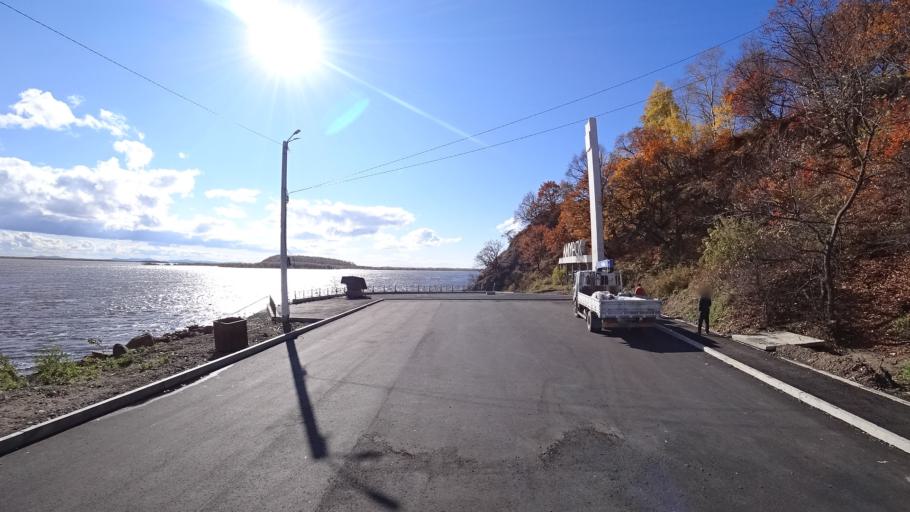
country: RU
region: Khabarovsk Krai
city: Amursk
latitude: 50.2146
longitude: 136.9061
